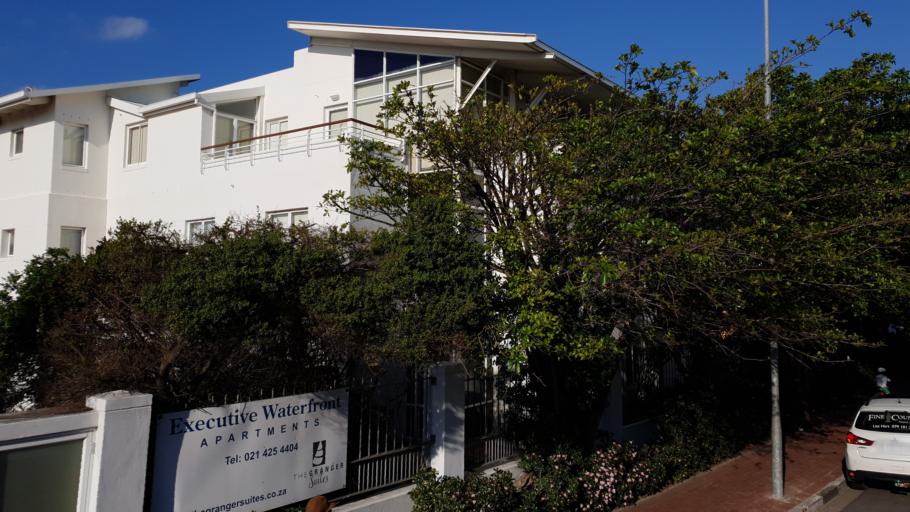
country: ZA
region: Western Cape
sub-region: City of Cape Town
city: Cape Town
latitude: -33.9001
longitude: 18.4117
